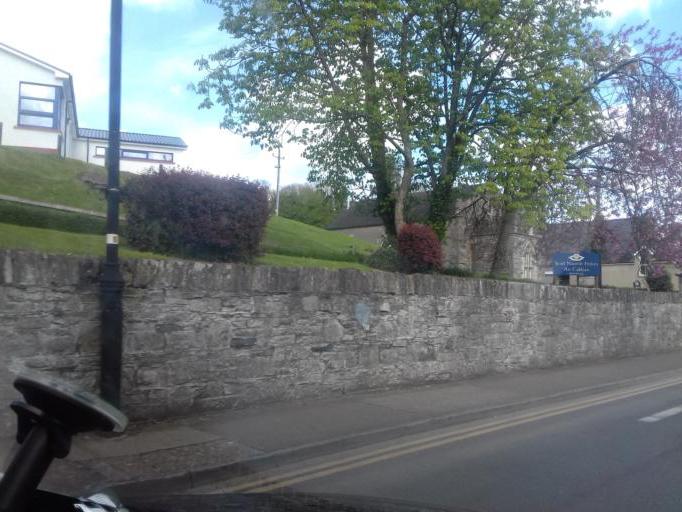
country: IE
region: Ulster
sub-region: An Cabhan
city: Cavan
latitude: 53.9910
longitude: -7.3628
